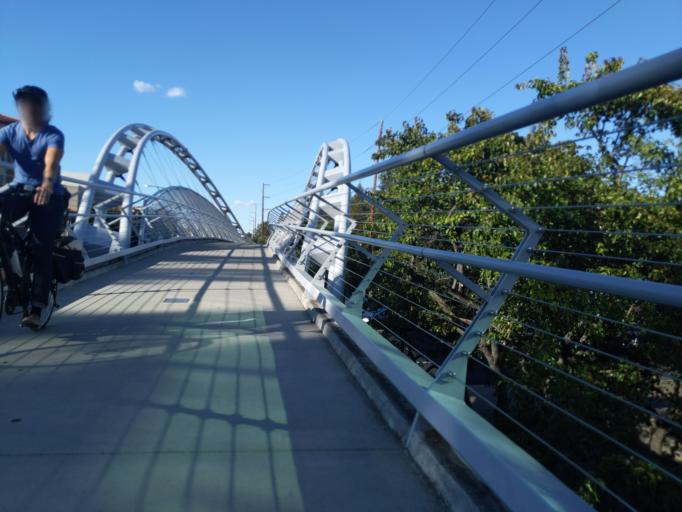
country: US
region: California
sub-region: Contra Costa County
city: Waldon
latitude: 37.9262
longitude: -122.0547
